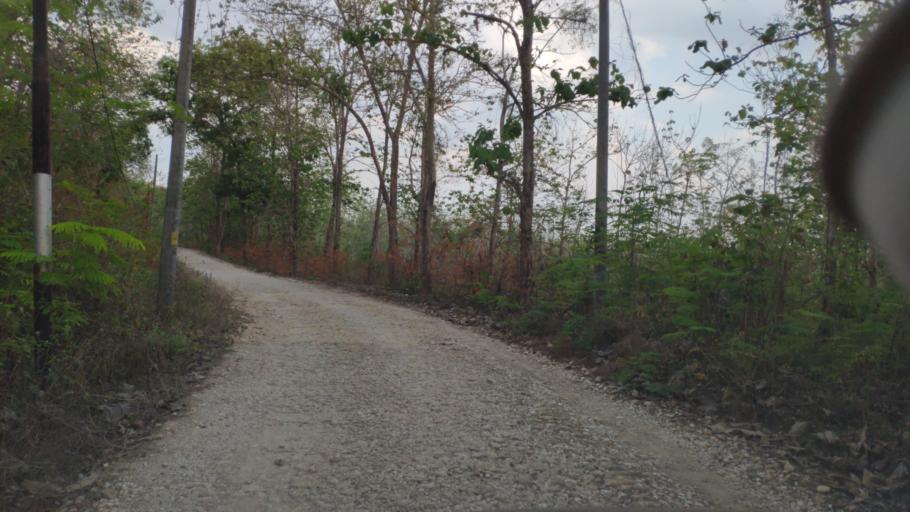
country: ID
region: Central Java
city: Semanggi
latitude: -7.0662
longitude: 111.4295
